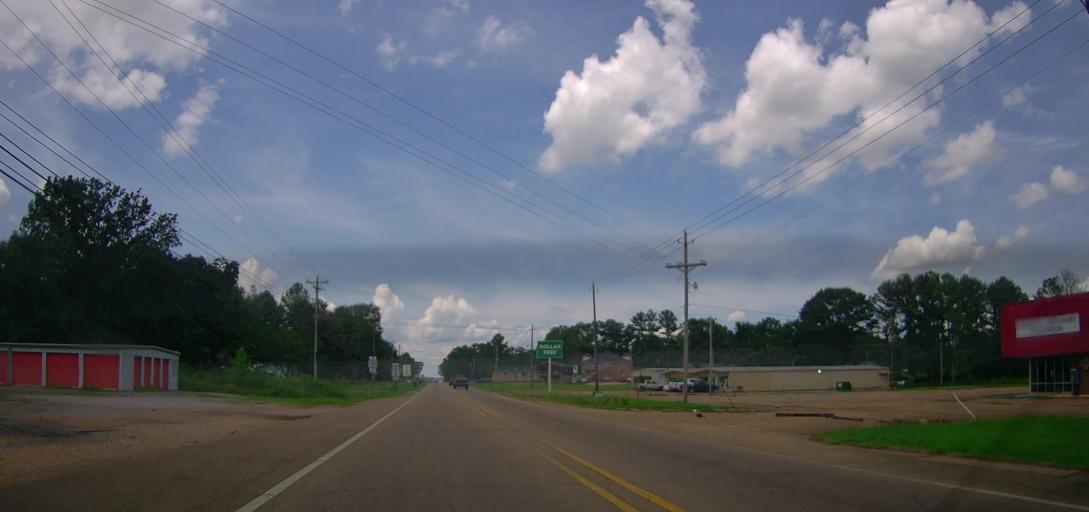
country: US
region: Mississippi
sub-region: Lee County
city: Shannon
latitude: 34.1280
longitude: -88.7193
